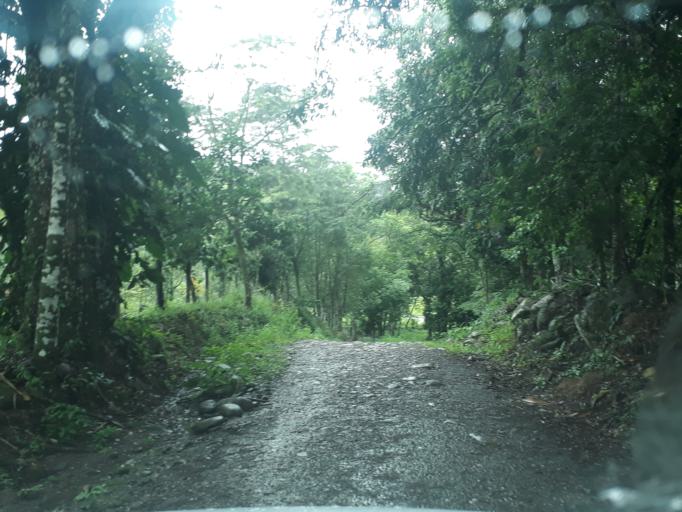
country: CO
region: Cundinamarca
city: Medina
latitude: 4.5209
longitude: -73.3578
